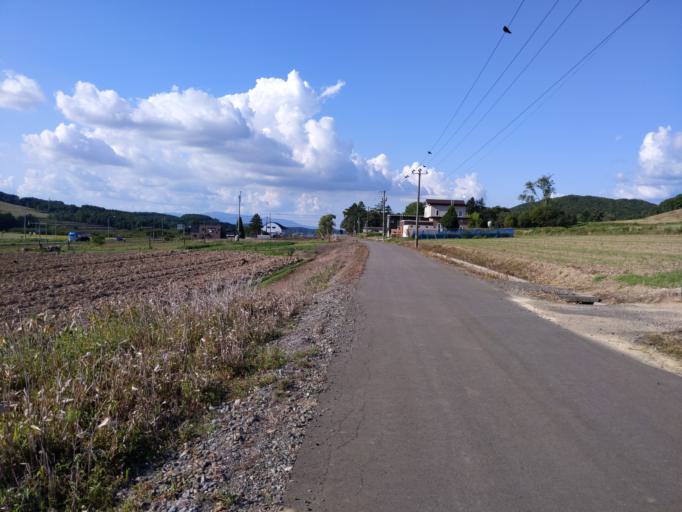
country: JP
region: Hokkaido
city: Iwamizawa
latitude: 43.1971
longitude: 141.8288
